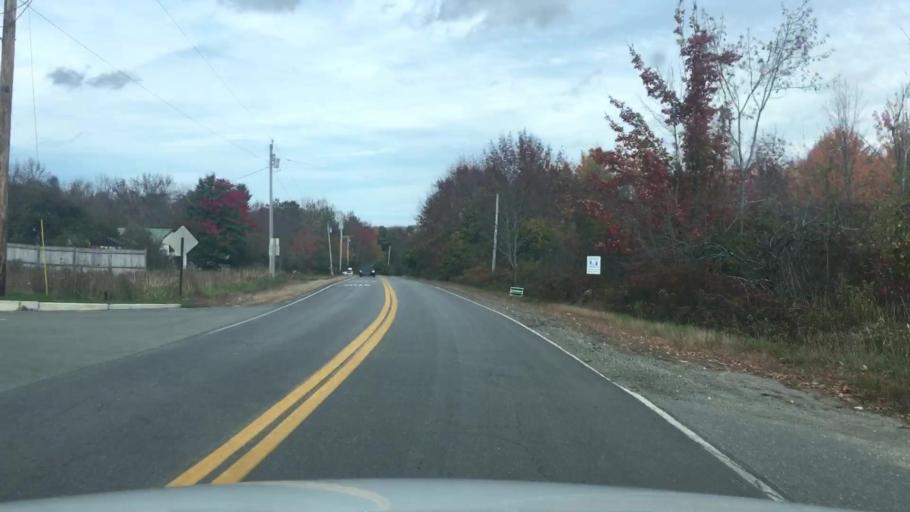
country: US
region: Maine
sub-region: Waldo County
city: Searsmont
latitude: 44.3982
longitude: -69.1343
